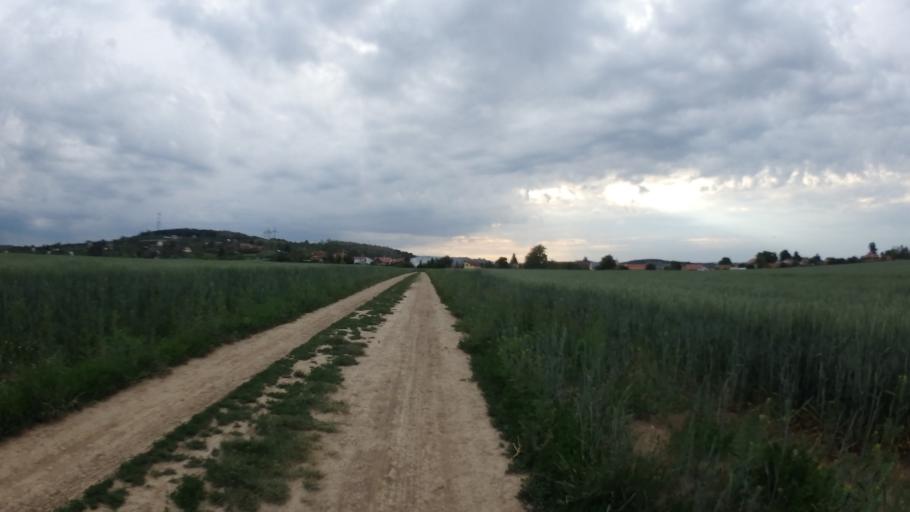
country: CZ
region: South Moravian
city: Moravany
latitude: 49.1390
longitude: 16.5591
